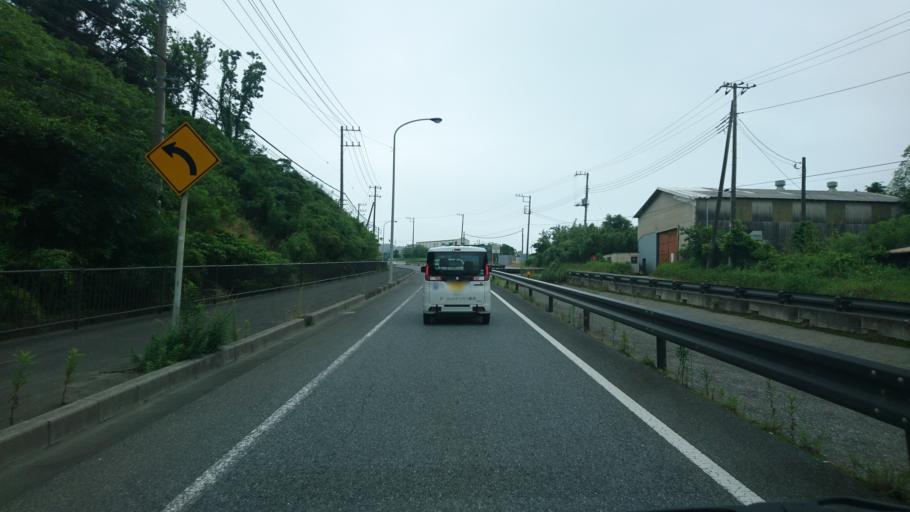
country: JP
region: Chiba
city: Kimitsu
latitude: 35.2467
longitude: 139.8873
